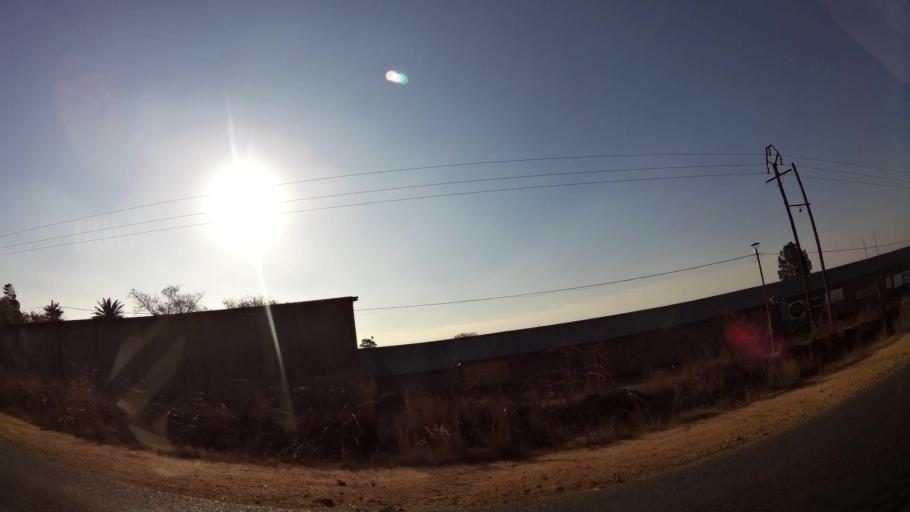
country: ZA
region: Gauteng
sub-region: West Rand District Municipality
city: Muldersdriseloop
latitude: -26.0242
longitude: 27.8719
